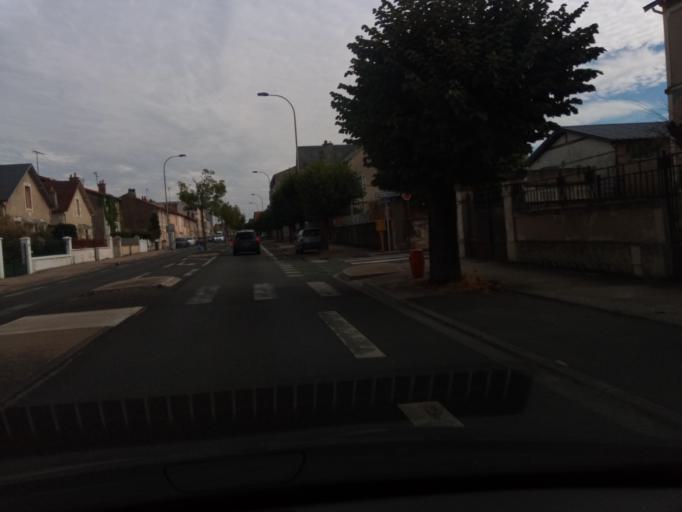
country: FR
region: Poitou-Charentes
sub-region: Departement de la Vienne
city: Biard
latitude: 46.5613
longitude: 0.3148
